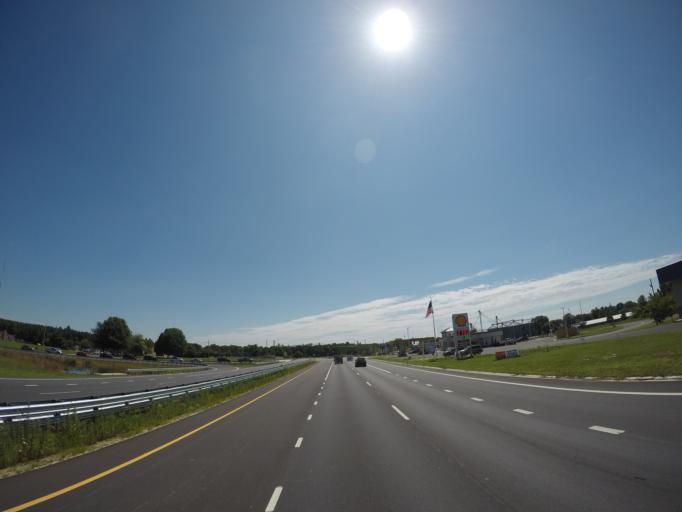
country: US
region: Maryland
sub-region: Caroline County
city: Ridgely
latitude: 38.9237
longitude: -75.9598
